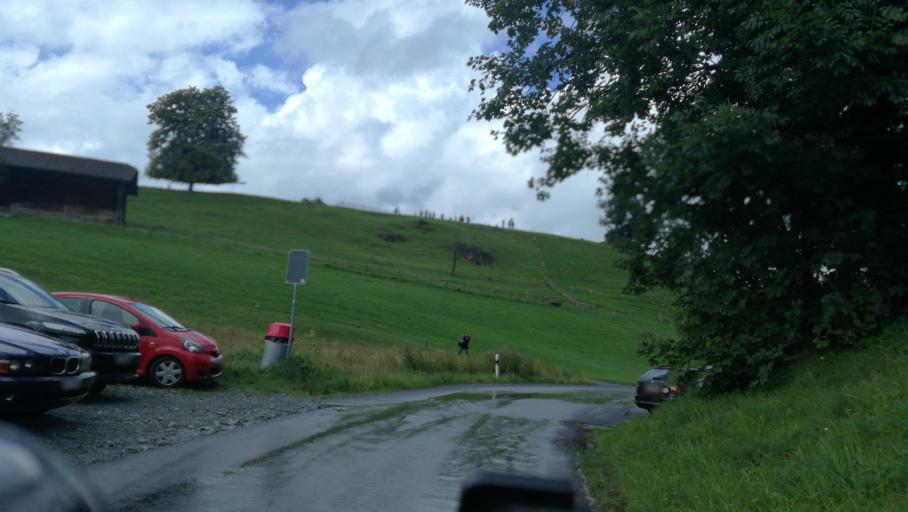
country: CH
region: Zug
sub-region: Zug
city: Zug
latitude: 47.1471
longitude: 8.5374
